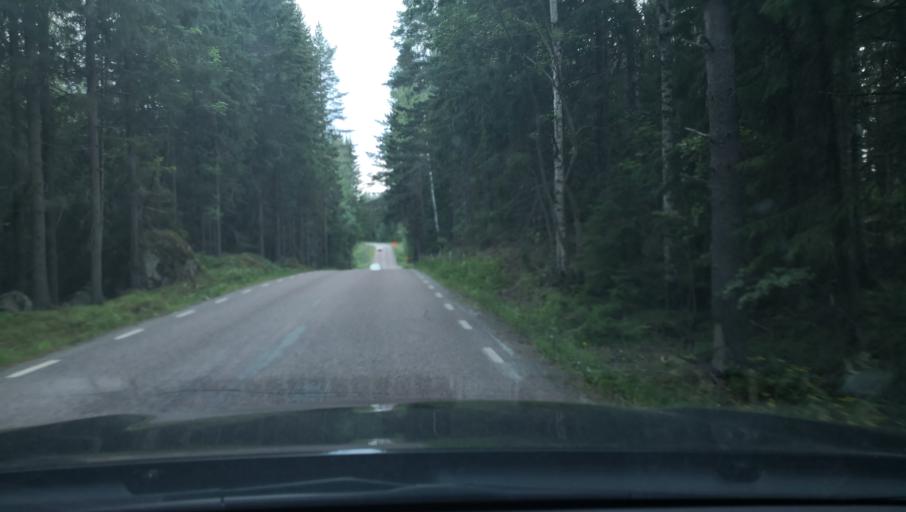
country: SE
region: Dalarna
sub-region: Smedjebackens Kommun
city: Smedjebacken
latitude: 60.0442
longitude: 15.5071
